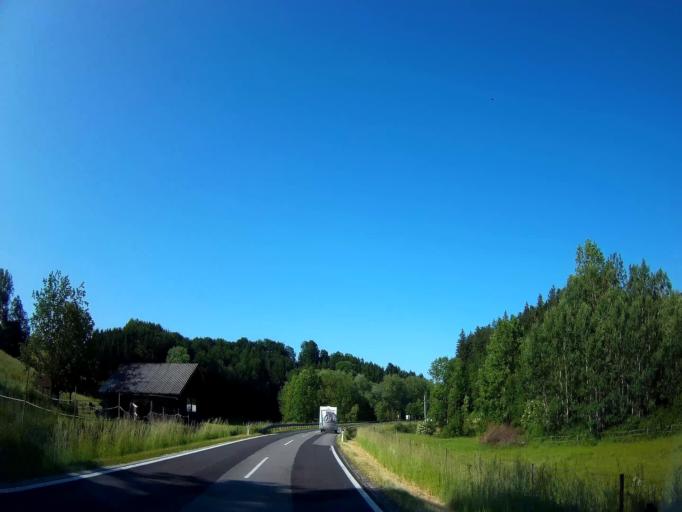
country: AT
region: Salzburg
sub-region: Politischer Bezirk Salzburg-Umgebung
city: Dorfbeuern
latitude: 48.1302
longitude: 13.0116
